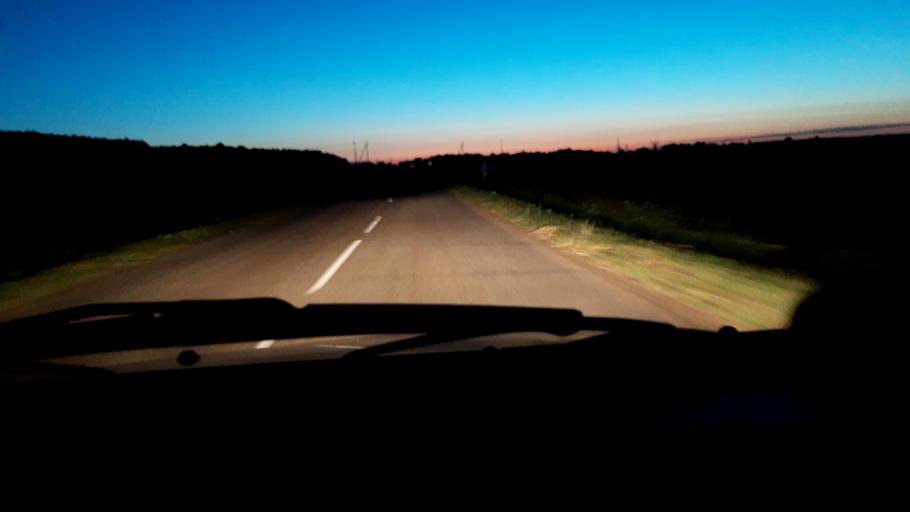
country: RU
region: Bashkortostan
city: Blagoveshchensk
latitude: 54.9340
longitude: 55.8993
